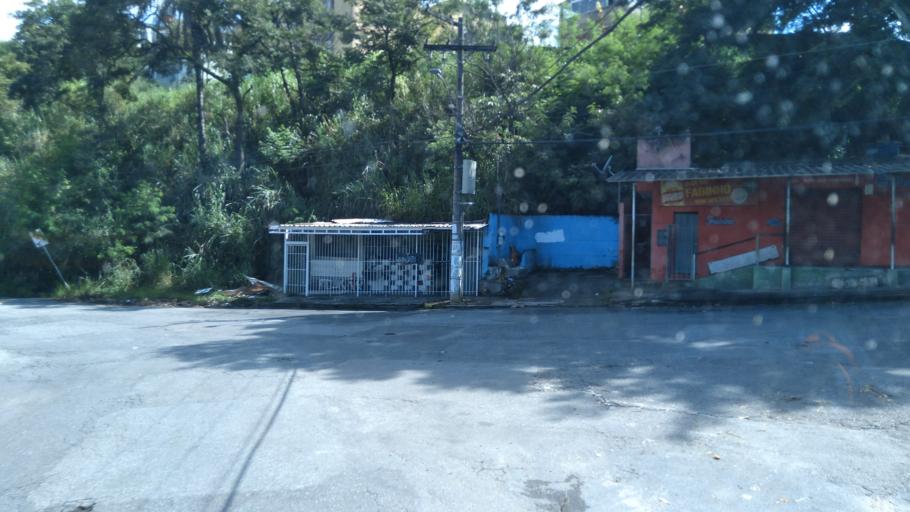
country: BR
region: Minas Gerais
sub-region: Santa Luzia
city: Santa Luzia
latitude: -19.8230
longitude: -43.9007
